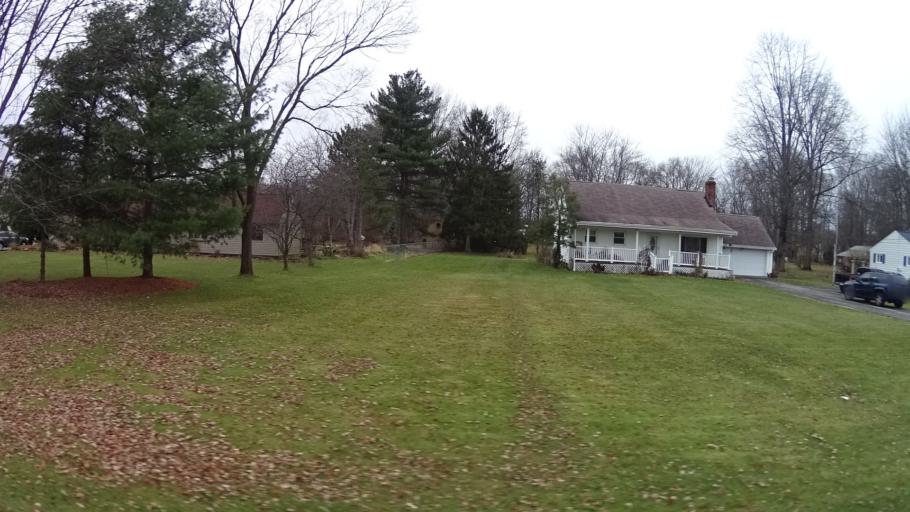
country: US
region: Ohio
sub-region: Lorain County
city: North Ridgeville
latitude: 41.3634
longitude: -81.9933
